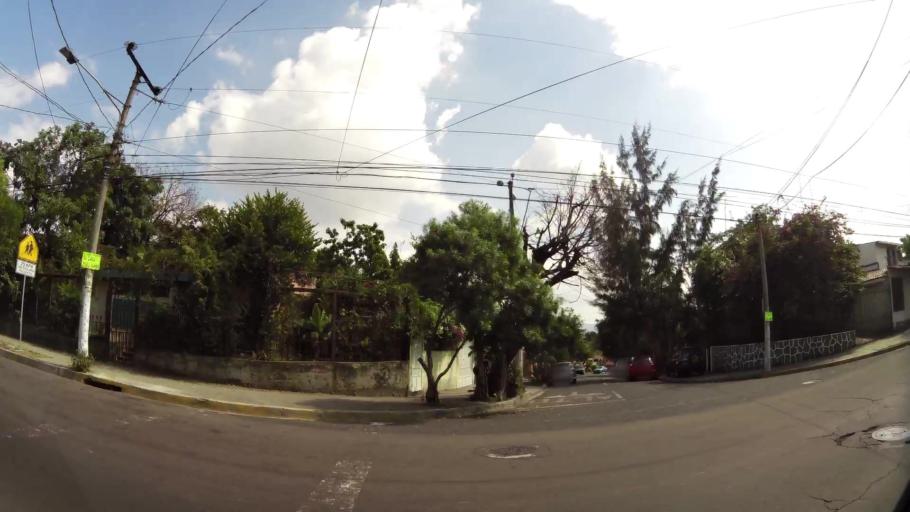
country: SV
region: San Salvador
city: Mejicanos
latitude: 13.7070
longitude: -89.2216
